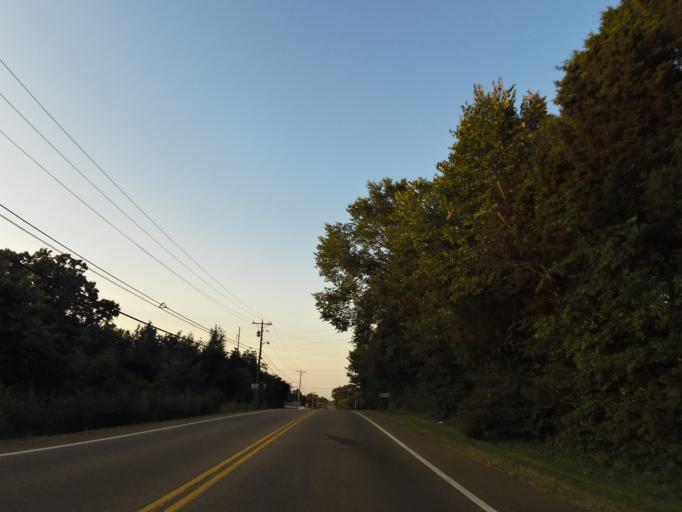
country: US
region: Tennessee
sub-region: Loudon County
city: Loudon
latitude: 35.7133
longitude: -84.3622
